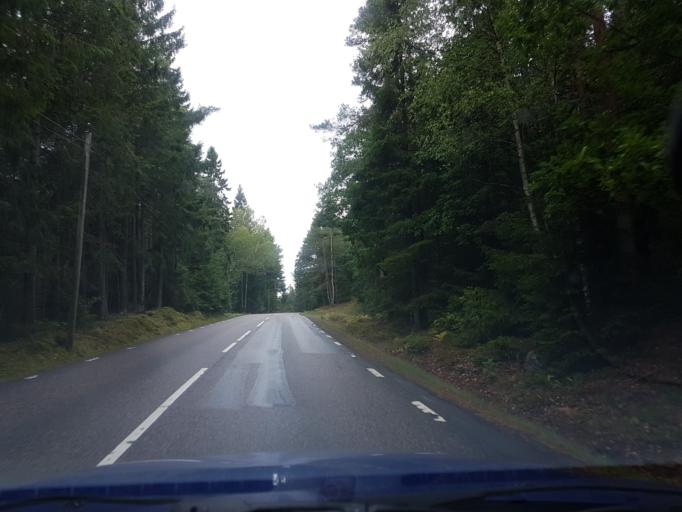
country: SE
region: Vaestra Goetaland
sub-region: Lerums Kommun
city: Grabo
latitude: 57.9183
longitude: 12.3195
